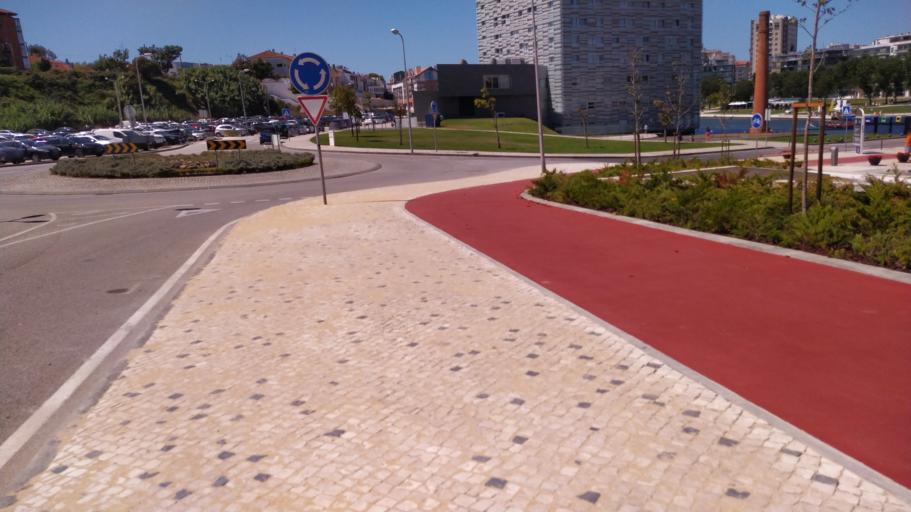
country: PT
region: Aveiro
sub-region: Aveiro
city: Aveiro
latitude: 40.6375
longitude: -8.6438
